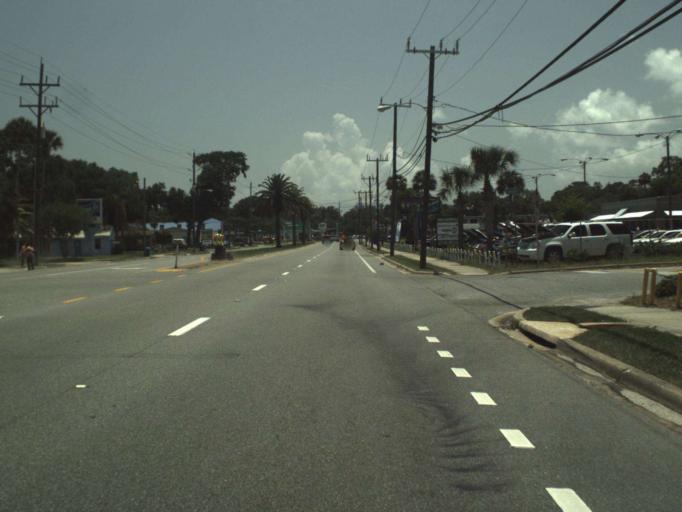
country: US
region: Florida
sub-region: Volusia County
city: New Smyrna Beach
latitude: 29.0455
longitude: -80.9350
